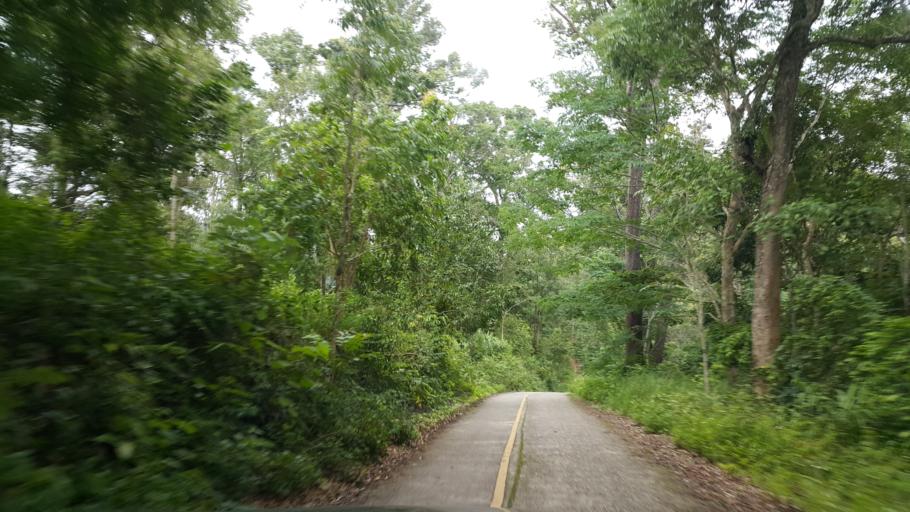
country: TH
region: Lampang
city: Mueang Pan
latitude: 18.8316
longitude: 99.3793
